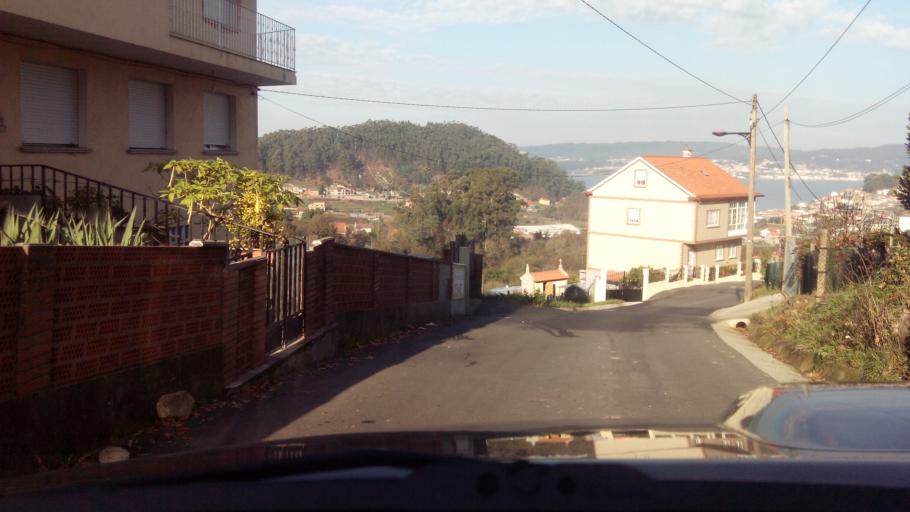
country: ES
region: Galicia
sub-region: Provincia de Pontevedra
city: Marin
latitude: 42.3576
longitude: -8.7328
